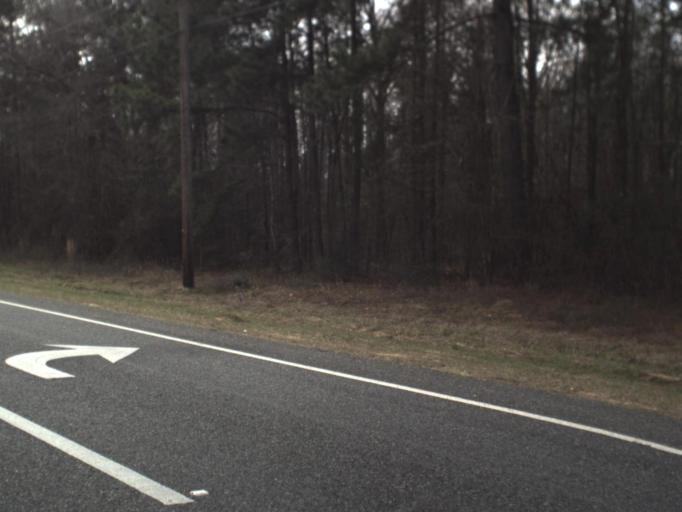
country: US
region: Florida
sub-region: Washington County
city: Chipley
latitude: 30.7352
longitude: -85.3864
